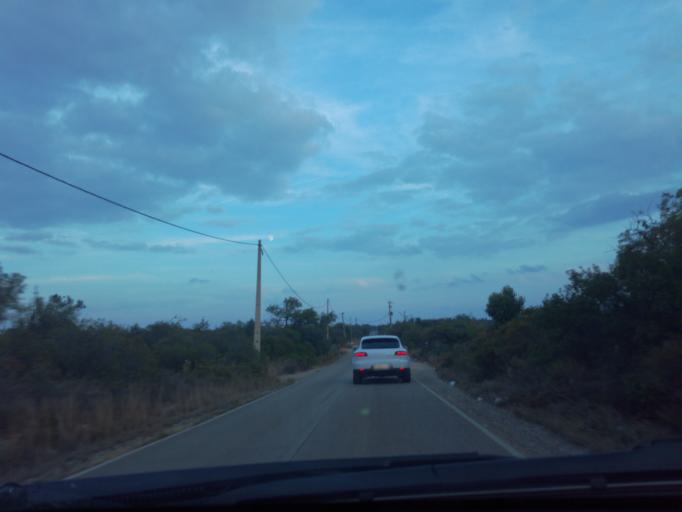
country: PT
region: Faro
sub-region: Olhao
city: Laranjeiro
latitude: 37.0802
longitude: -7.8331
